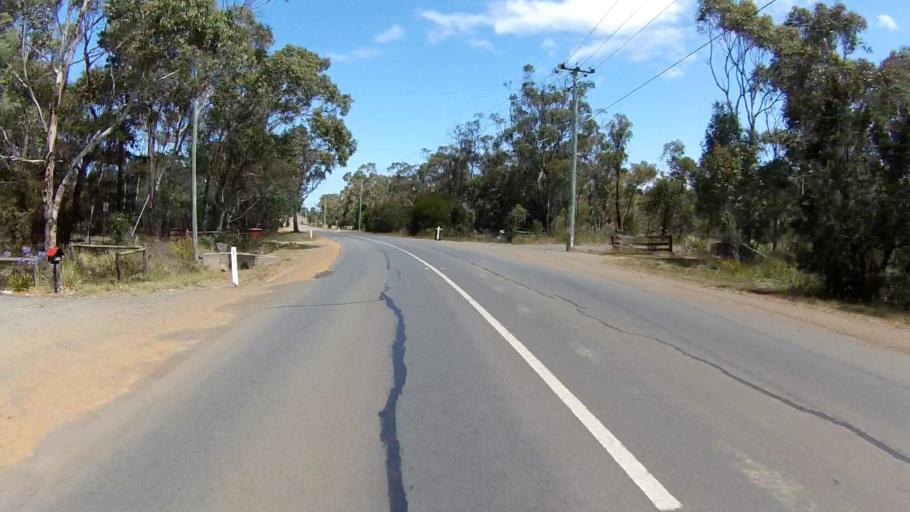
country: AU
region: Tasmania
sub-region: Clarence
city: Sandford
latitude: -42.9457
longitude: 147.4826
